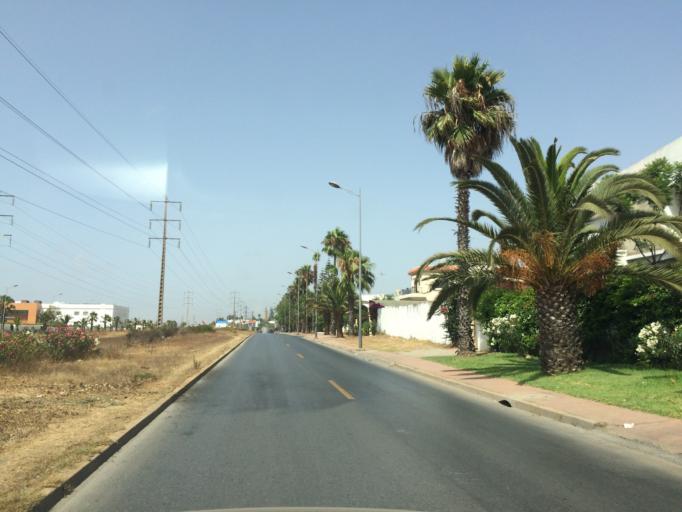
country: MA
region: Rabat-Sale-Zemmour-Zaer
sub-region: Skhirate-Temara
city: Temara
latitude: 33.9674
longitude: -6.8680
